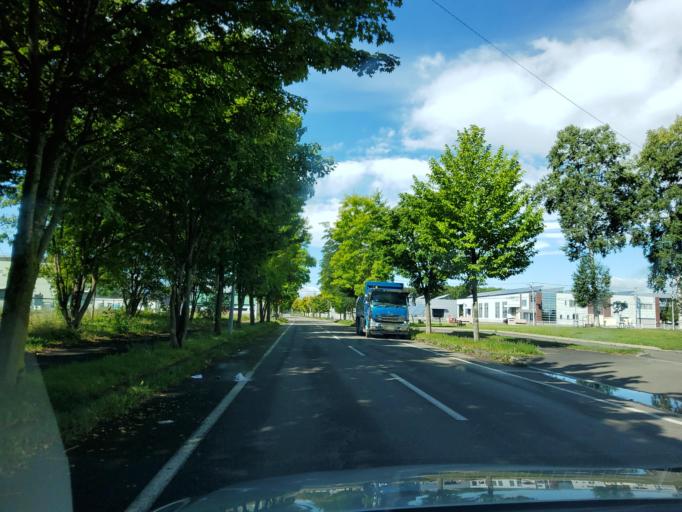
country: JP
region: Hokkaido
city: Otofuke
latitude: 42.9857
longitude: 143.1803
